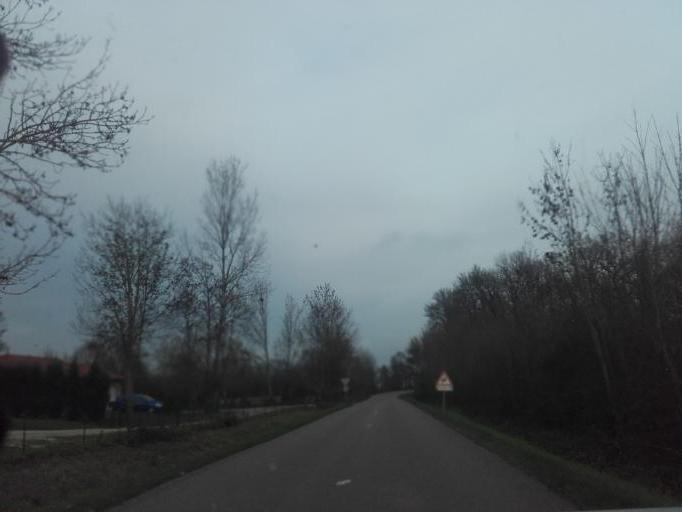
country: FR
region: Bourgogne
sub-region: Departement de la Cote-d'Or
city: Beaune
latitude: 46.9944
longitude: 4.9413
